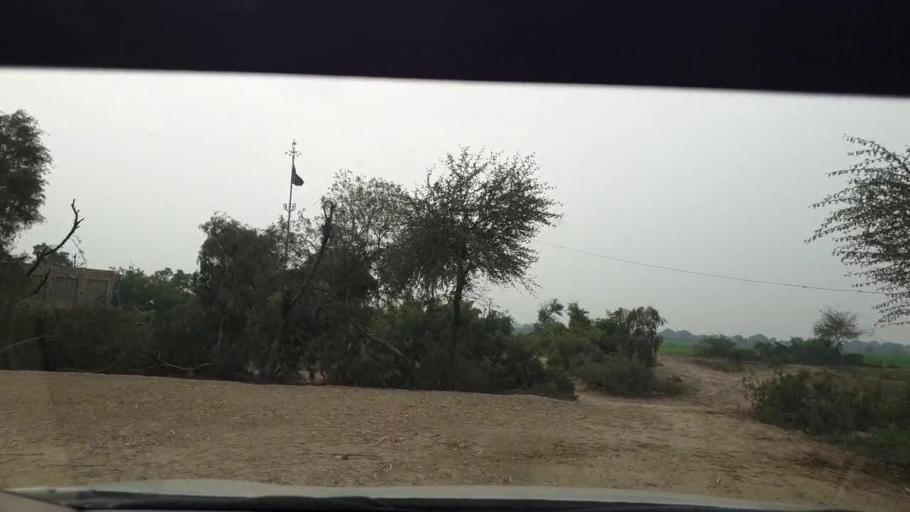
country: PK
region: Sindh
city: Berani
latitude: 25.8606
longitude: 68.8386
